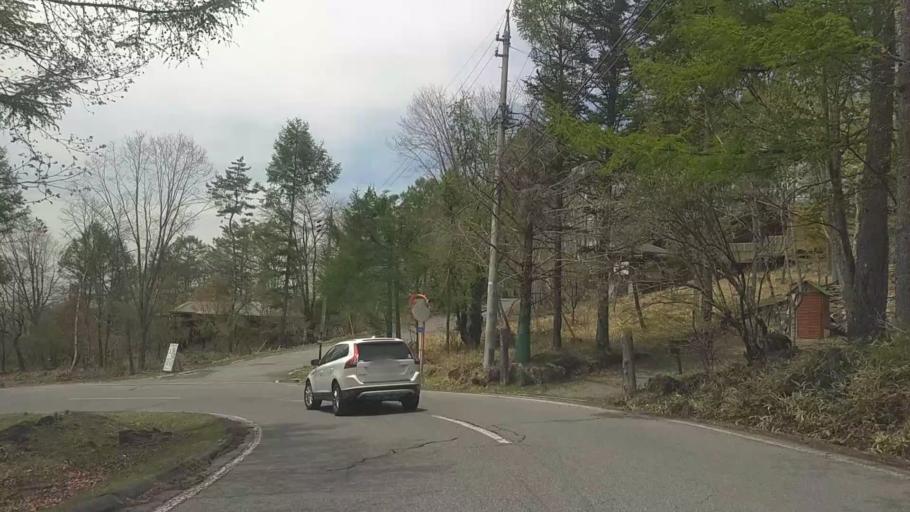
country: JP
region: Nagano
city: Chino
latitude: 36.0471
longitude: 138.3016
